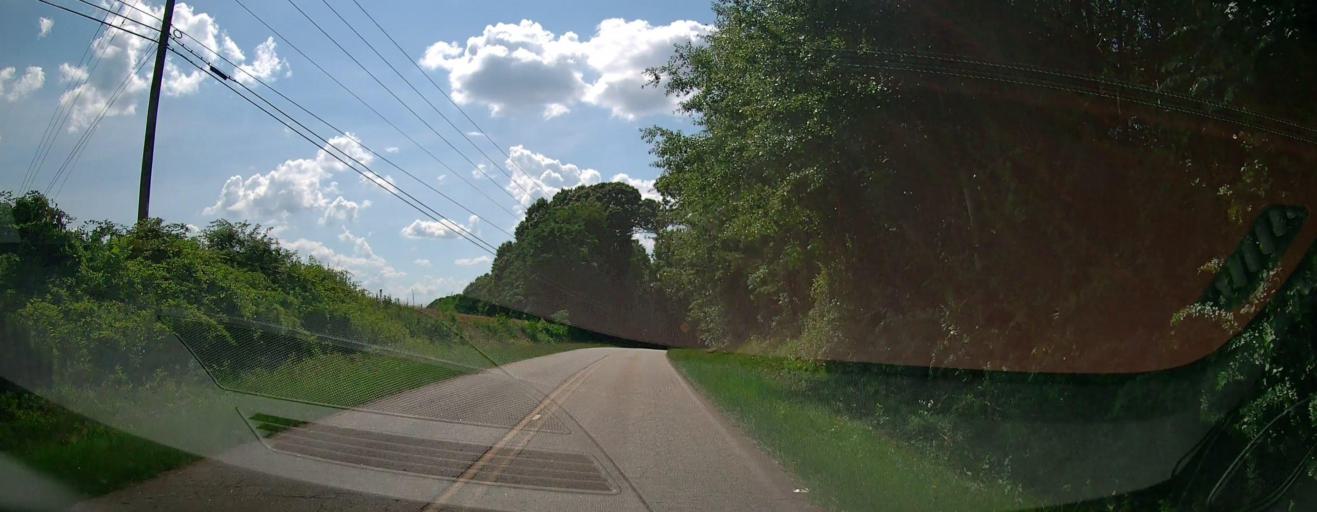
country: US
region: Georgia
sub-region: Spalding County
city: East Griffin
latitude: 33.2277
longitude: -84.1258
